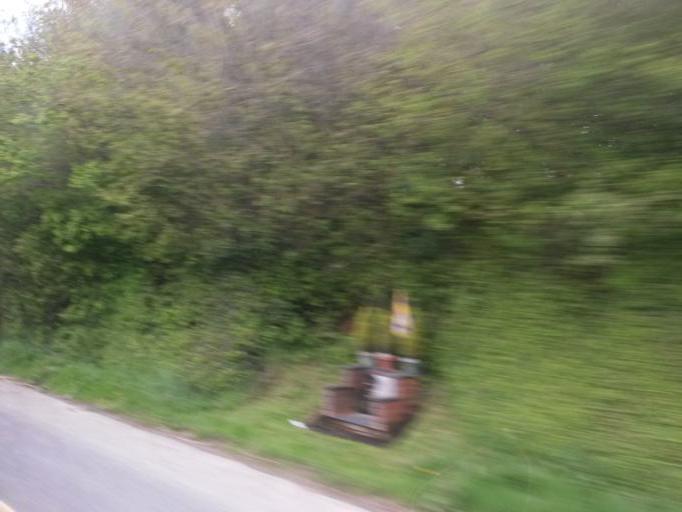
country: IE
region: Leinster
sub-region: Loch Garman
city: Enniscorthy
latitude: 52.4420
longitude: -6.5402
